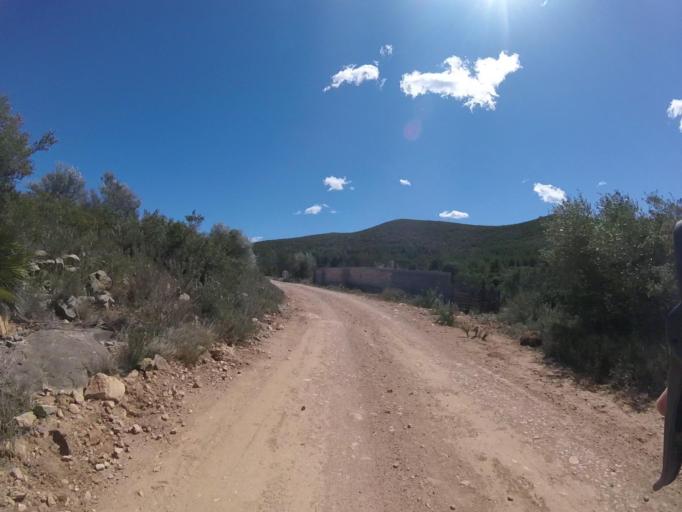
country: ES
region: Valencia
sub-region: Provincia de Castello
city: Orpesa/Oropesa del Mar
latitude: 40.1660
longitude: 0.1340
